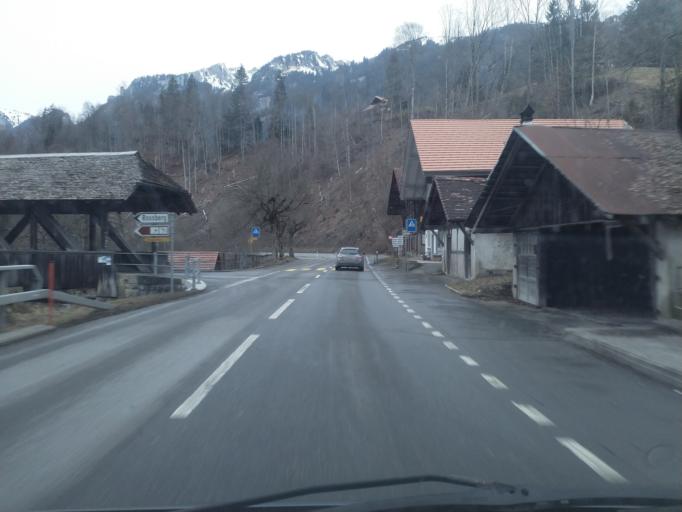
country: CH
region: Bern
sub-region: Obersimmental-Saanen District
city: Boltigen
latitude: 46.6548
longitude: 7.4400
